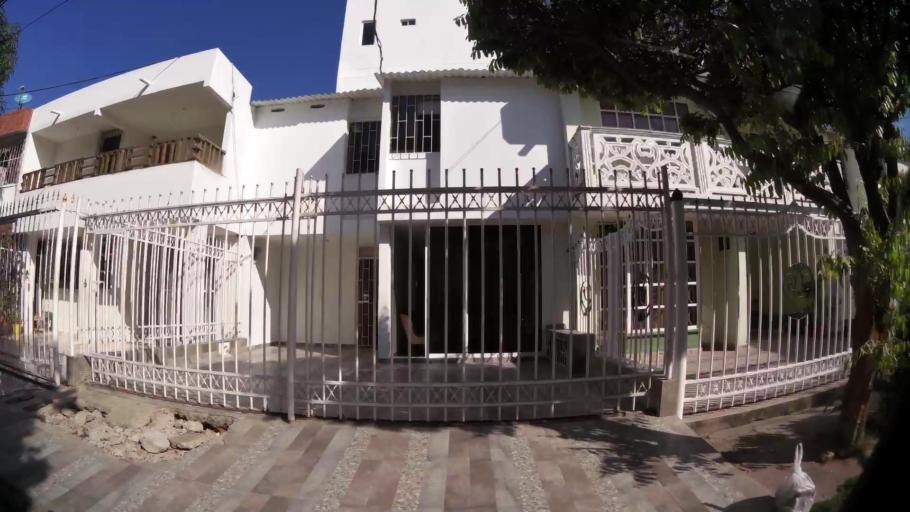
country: CO
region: Bolivar
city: Cartagena
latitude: 10.3927
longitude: -75.4961
